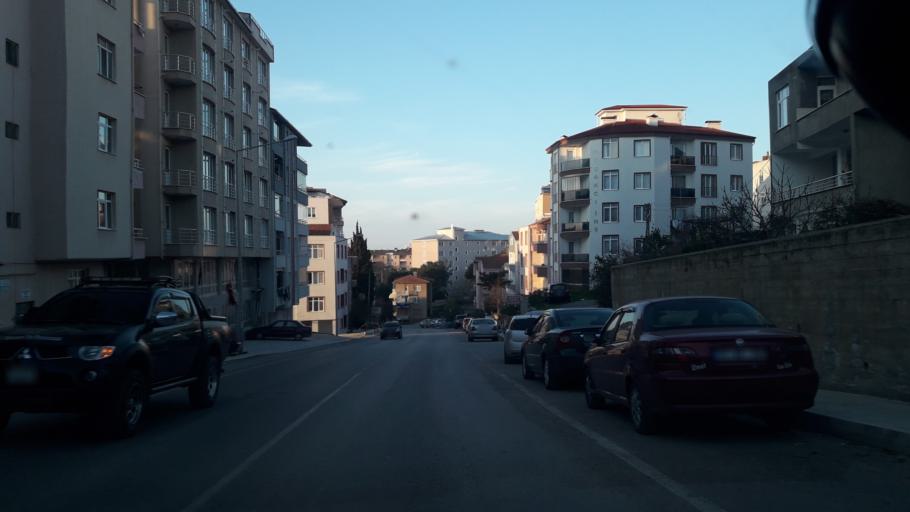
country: TR
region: Sinop
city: Sinop
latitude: 42.0259
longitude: 35.1611
